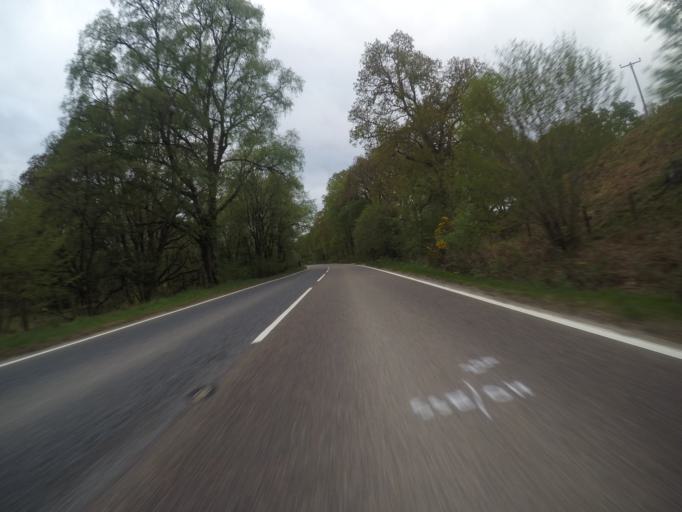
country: GB
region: Scotland
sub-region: Highland
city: Spean Bridge
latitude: 56.8941
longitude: -4.8892
